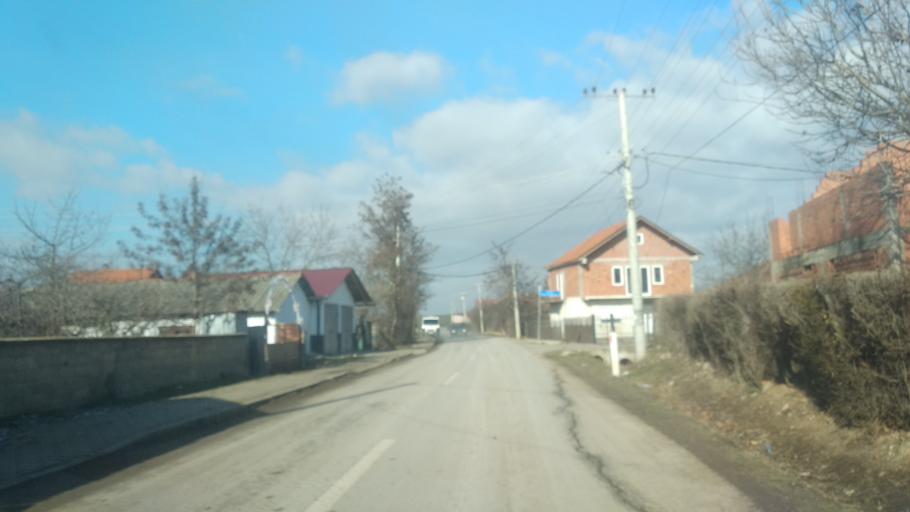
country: XK
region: Pristina
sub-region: Lipjan
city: Lipljan
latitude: 42.5480
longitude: 21.1794
